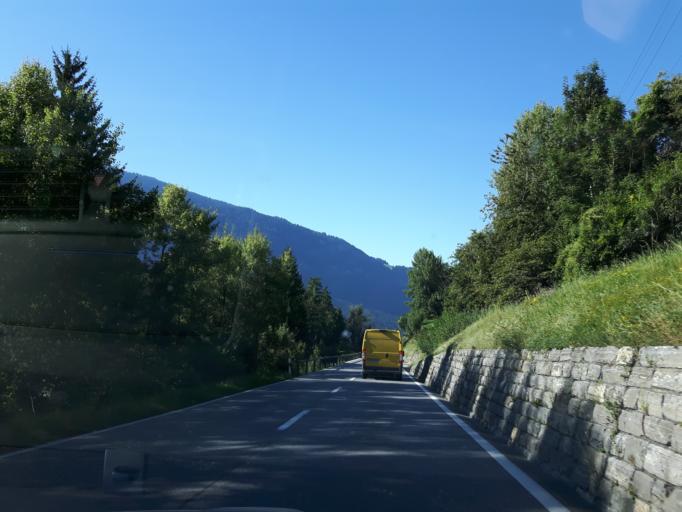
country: CH
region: Grisons
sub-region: Surselva District
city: Laax
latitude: 46.7954
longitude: 9.2520
